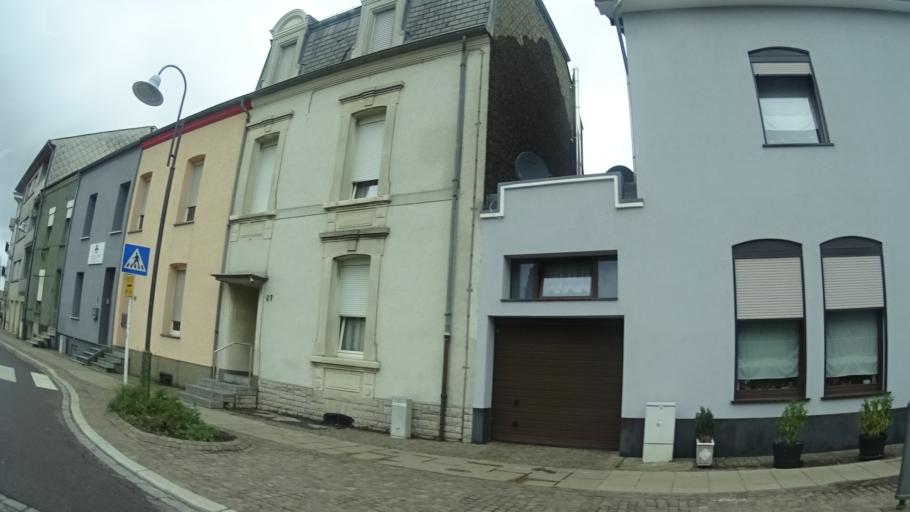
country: LU
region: Luxembourg
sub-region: Canton d'Esch-sur-Alzette
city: Bettembourg
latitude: 49.5163
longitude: 6.1031
